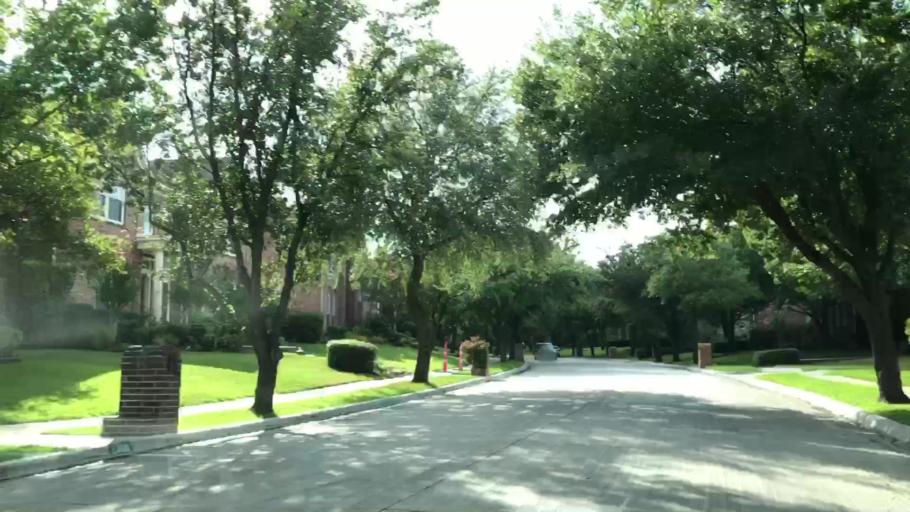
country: US
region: Texas
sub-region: Dallas County
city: Coppell
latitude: 32.9144
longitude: -96.9750
